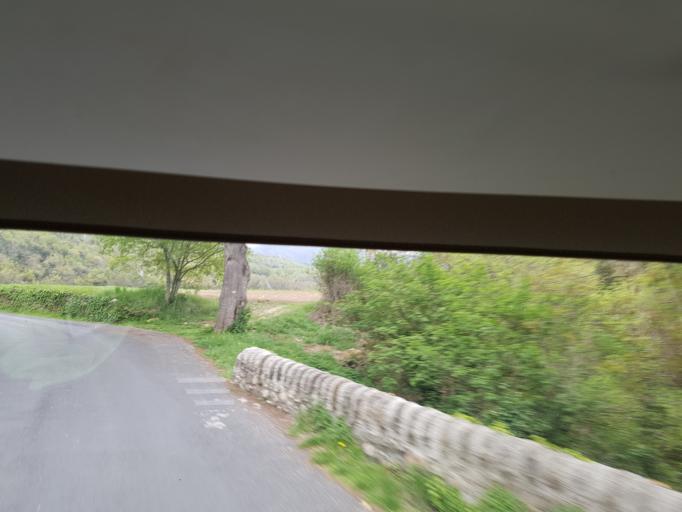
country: FR
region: Languedoc-Roussillon
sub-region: Departement des Pyrenees-Orientales
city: Ria-Sirach
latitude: 42.5945
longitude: 2.4166
